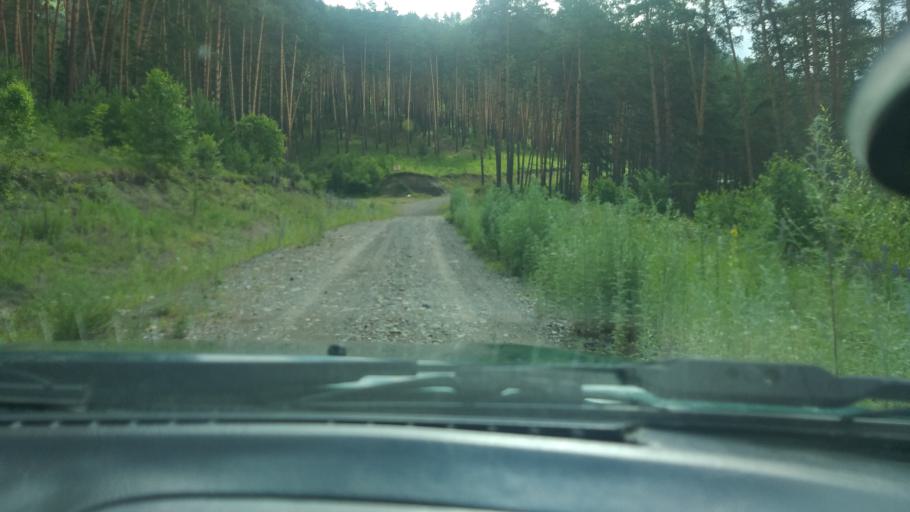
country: RU
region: Altay
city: Chemal
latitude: 51.3907
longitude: 86.0508
